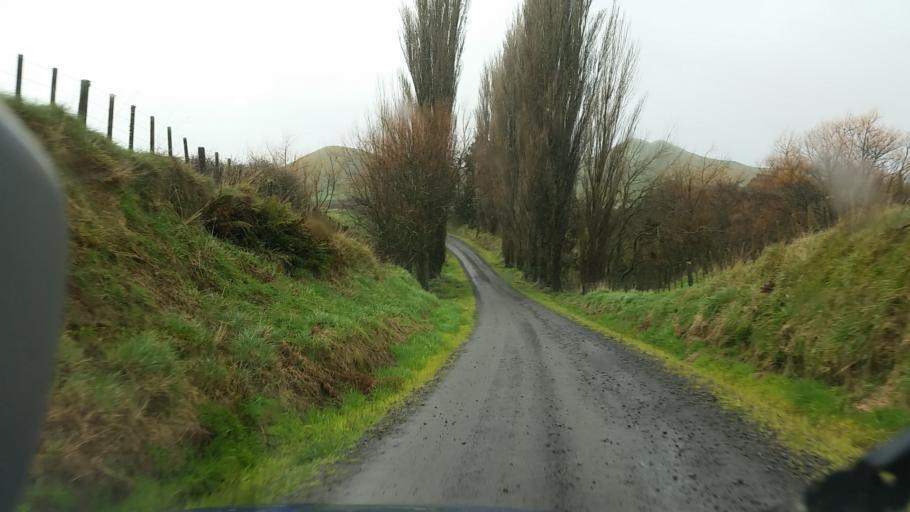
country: NZ
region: Taranaki
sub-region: South Taranaki District
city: Eltham
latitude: -39.3482
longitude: 174.4371
